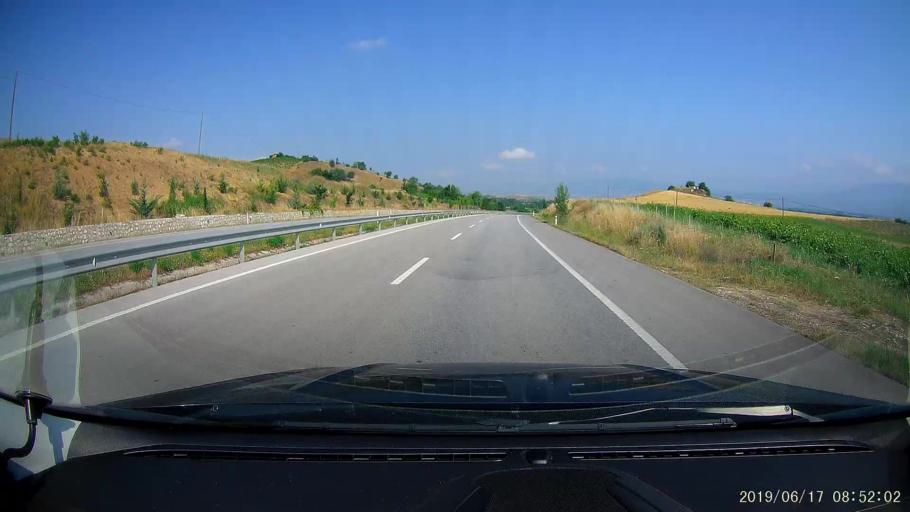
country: TR
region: Tokat
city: Erbaa
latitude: 40.6926
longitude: 36.5035
